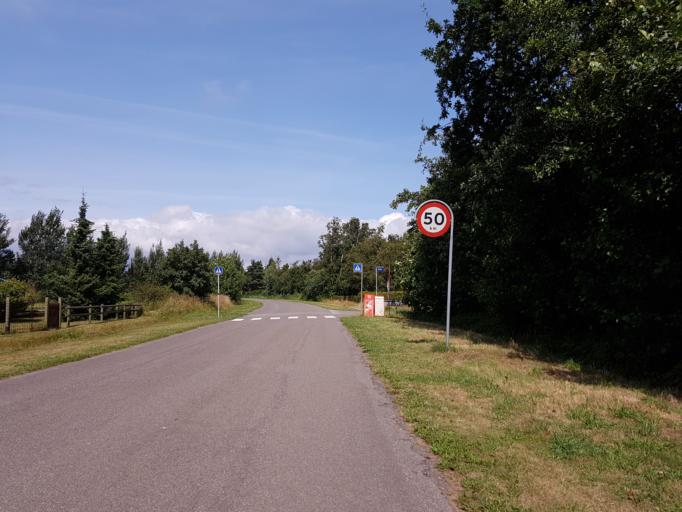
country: DK
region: Zealand
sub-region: Guldborgsund Kommune
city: Nykobing Falster
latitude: 54.5968
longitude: 11.9649
